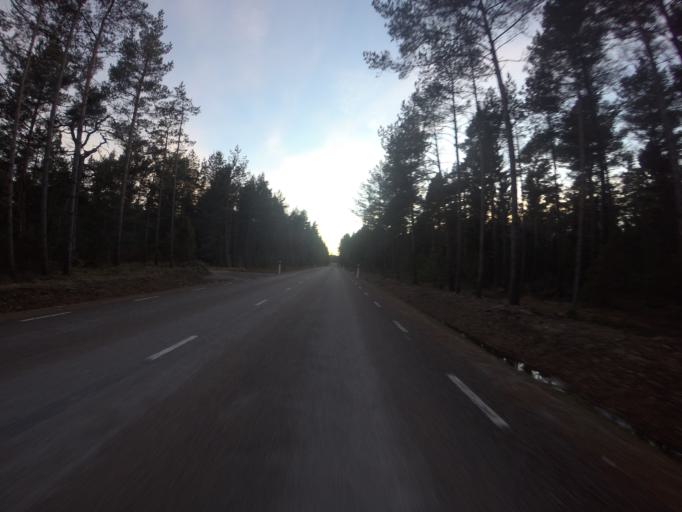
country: EE
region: Saare
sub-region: Orissaare vald
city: Orissaare
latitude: 58.5904
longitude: 22.7130
